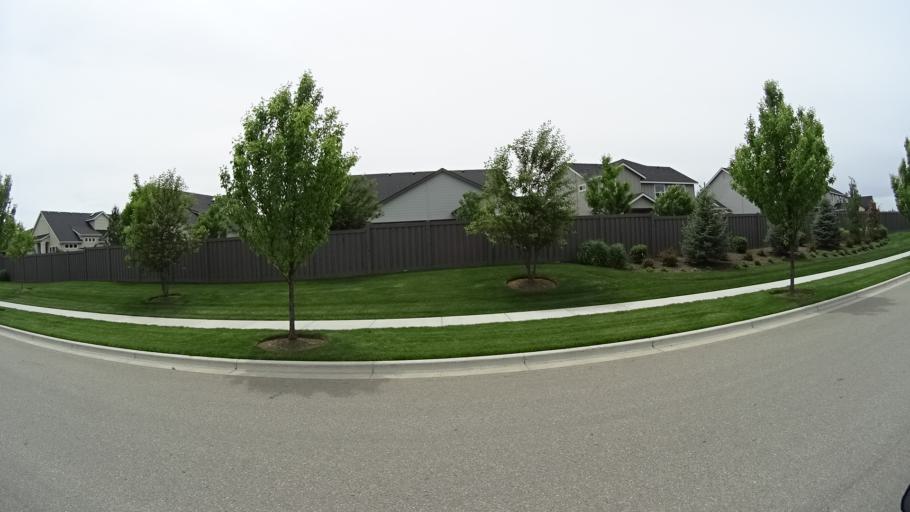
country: US
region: Idaho
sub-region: Ada County
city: Meridian
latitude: 43.5546
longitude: -116.3497
